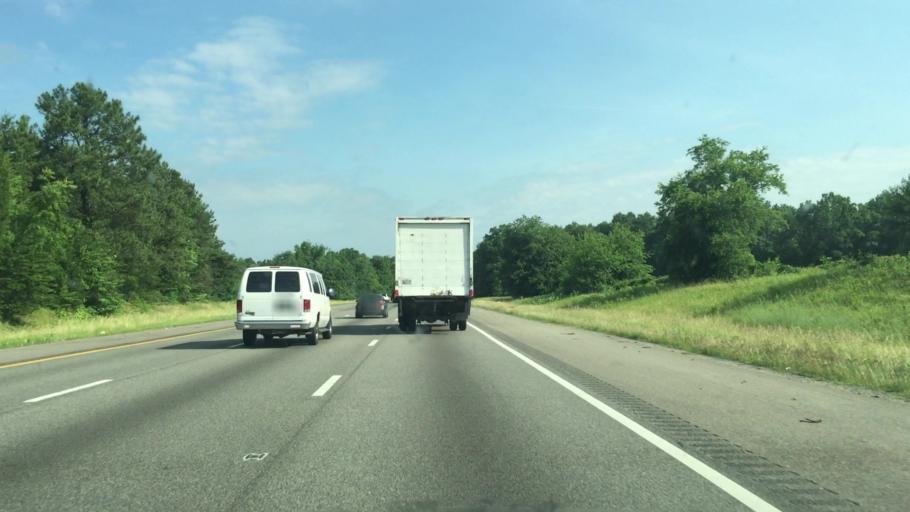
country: US
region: Virginia
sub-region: Spotsylvania County
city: Spotsylvania Courthouse
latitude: 38.0791
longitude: -77.5135
